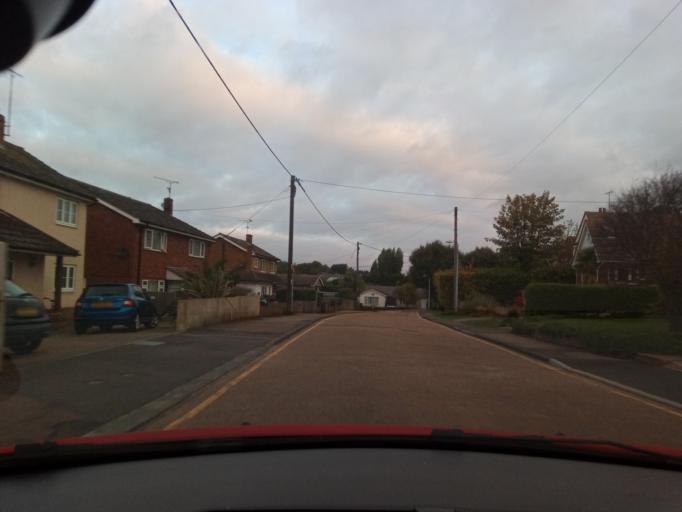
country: GB
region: England
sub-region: Essex
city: West Mersea
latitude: 51.7751
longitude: 0.9213
